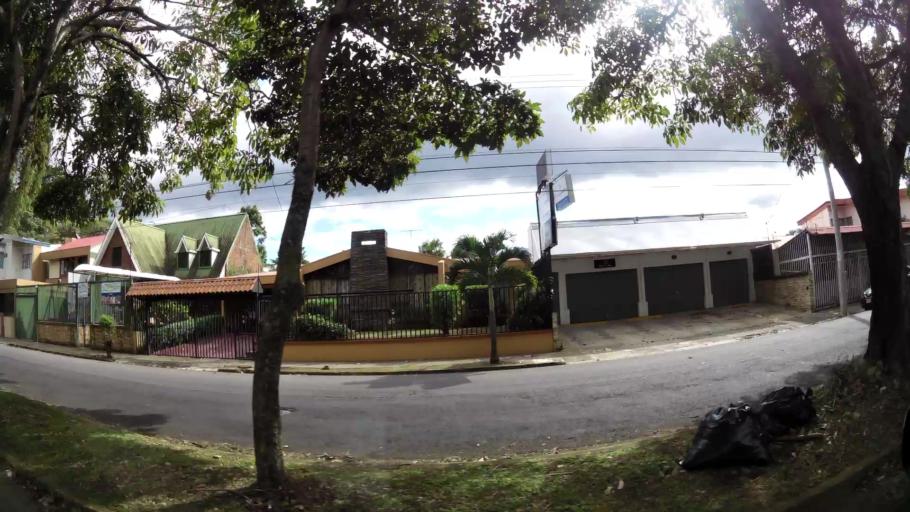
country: CR
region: San Jose
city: San Rafael
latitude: 9.9471
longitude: -84.1263
